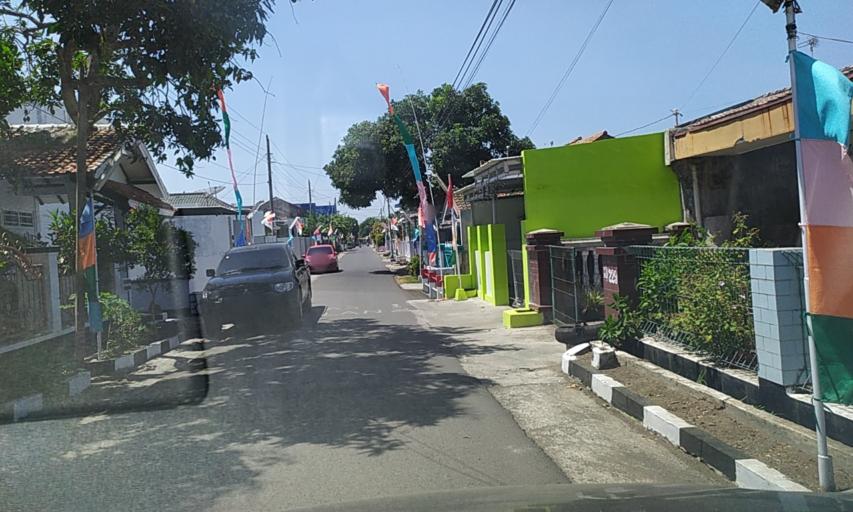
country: ID
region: Central Java
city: Karangbadar Kidul
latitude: -7.7166
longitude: 109.0066
